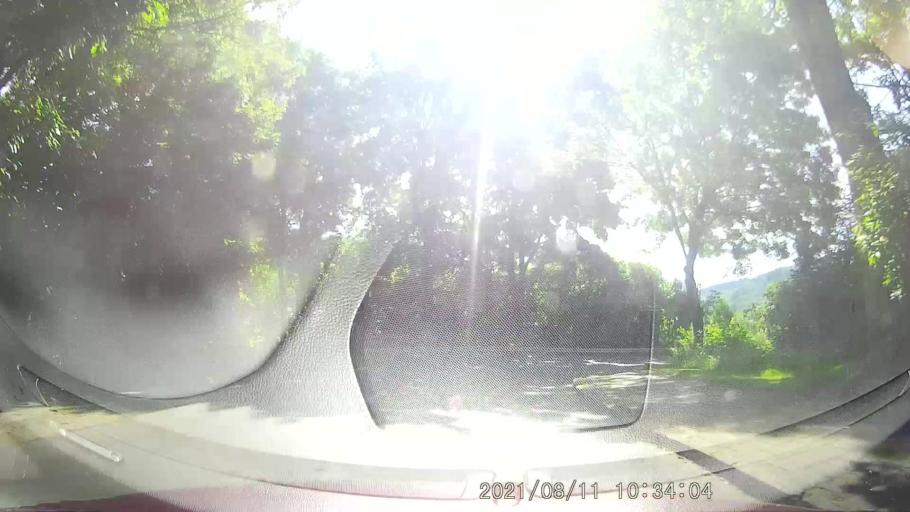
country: PL
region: Lower Silesian Voivodeship
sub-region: Powiat klodzki
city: Szczytna
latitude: 50.4117
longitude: 16.4481
